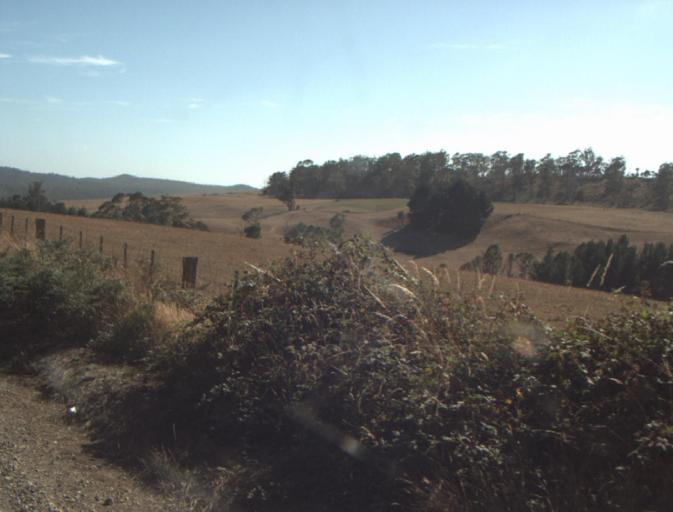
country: AU
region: Tasmania
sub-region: Launceston
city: Mayfield
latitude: -41.1659
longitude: 147.2122
